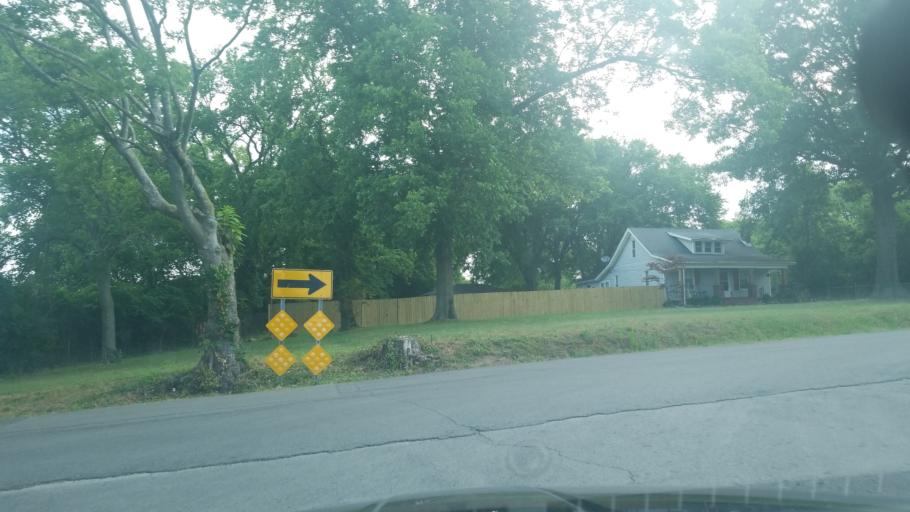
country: US
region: Tennessee
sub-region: Davidson County
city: Nashville
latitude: 36.2290
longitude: -86.7459
